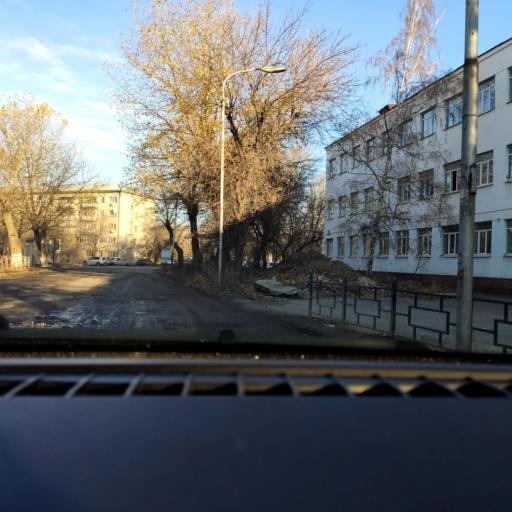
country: RU
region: Voronezj
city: Voronezh
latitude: 51.6348
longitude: 39.2503
